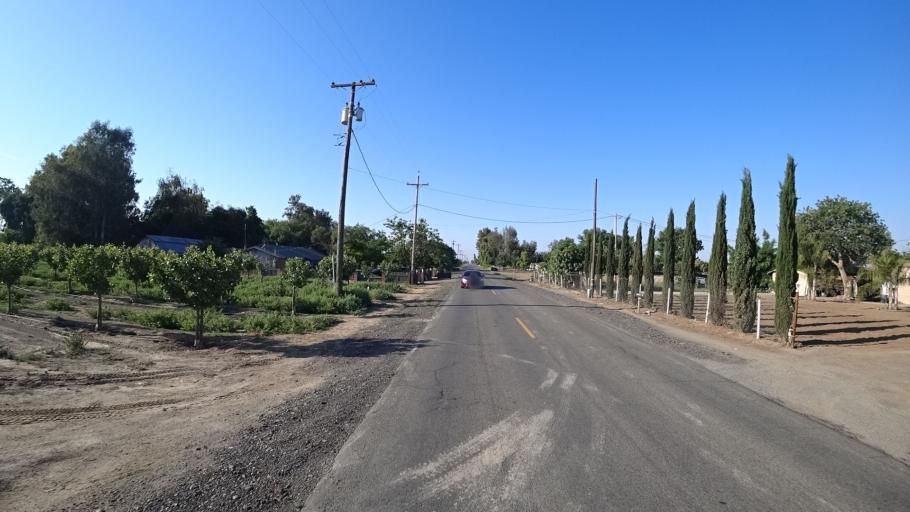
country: US
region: California
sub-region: Kings County
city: Lemoore
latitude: 36.2800
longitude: -119.7447
